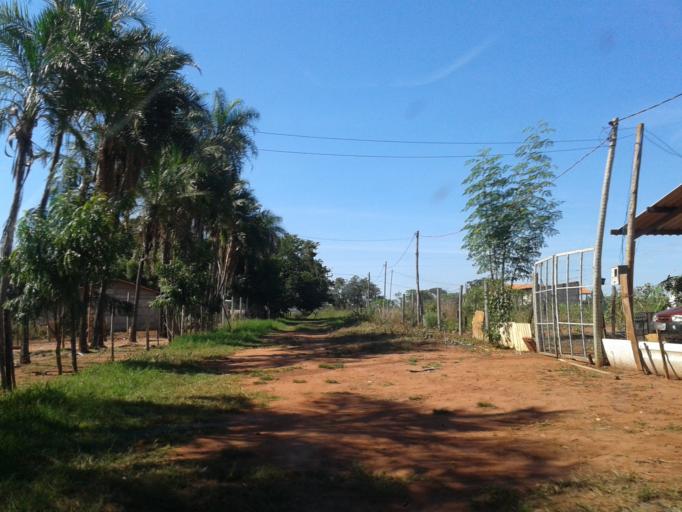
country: BR
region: Minas Gerais
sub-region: Santa Vitoria
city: Santa Vitoria
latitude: -19.0061
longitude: -50.3256
